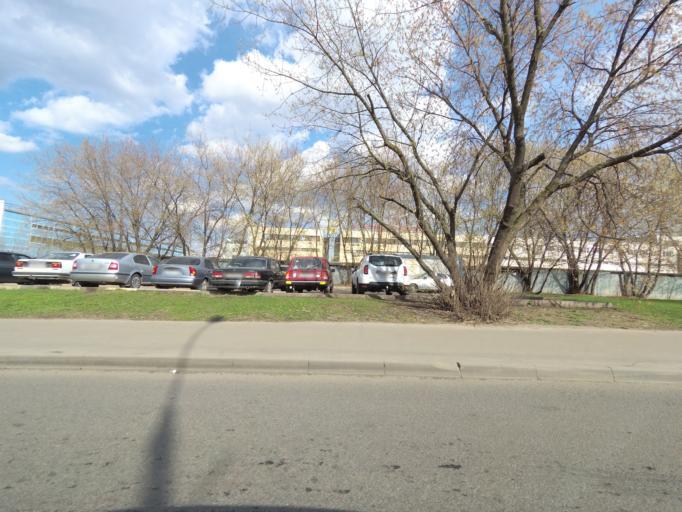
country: RU
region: Moscow
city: Gol'yanovo
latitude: 55.8035
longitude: 37.8304
